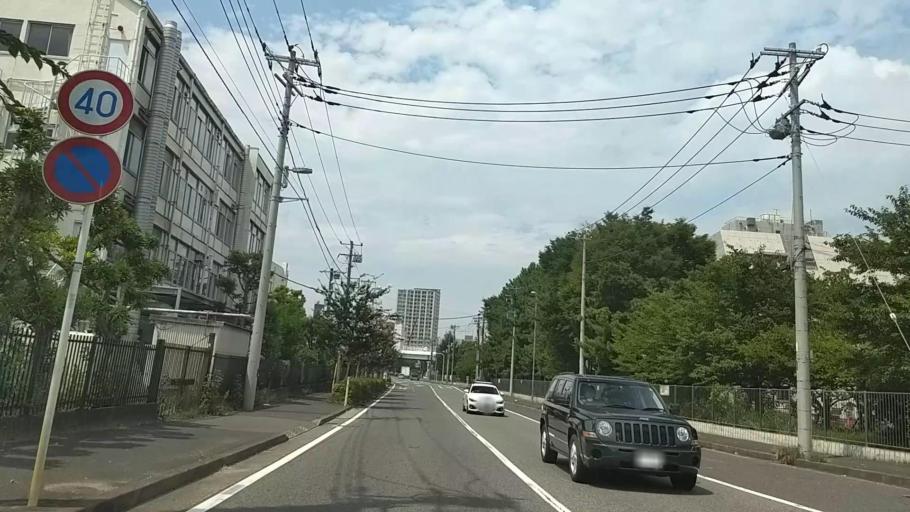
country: JP
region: Kanagawa
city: Yokohama
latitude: 35.4740
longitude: 139.6389
